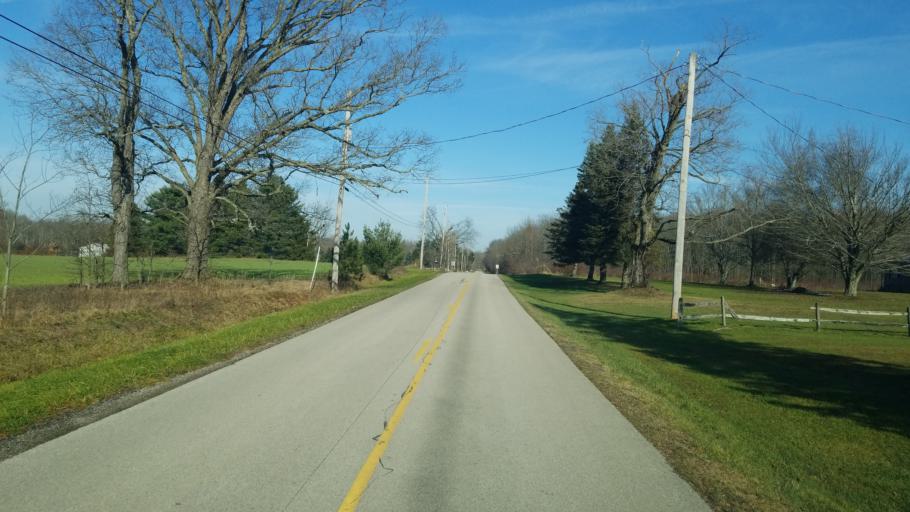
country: US
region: Ohio
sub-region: Ashtabula County
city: Jefferson
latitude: 41.7537
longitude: -80.7897
